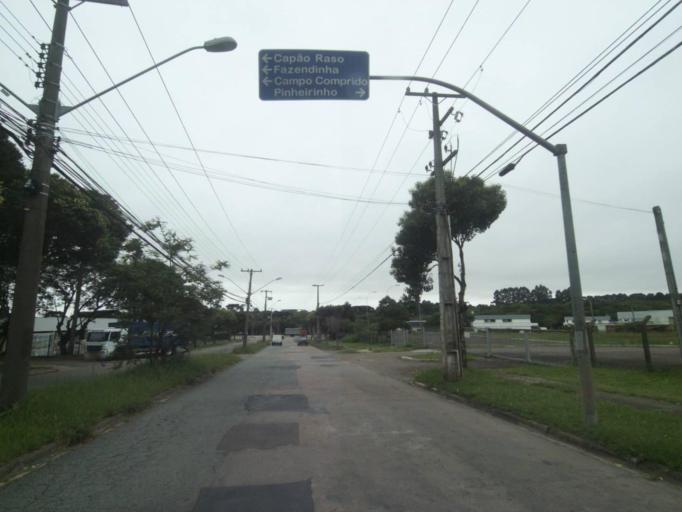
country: BR
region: Parana
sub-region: Sao Jose Dos Pinhais
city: Sao Jose dos Pinhais
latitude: -25.5301
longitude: -49.3140
